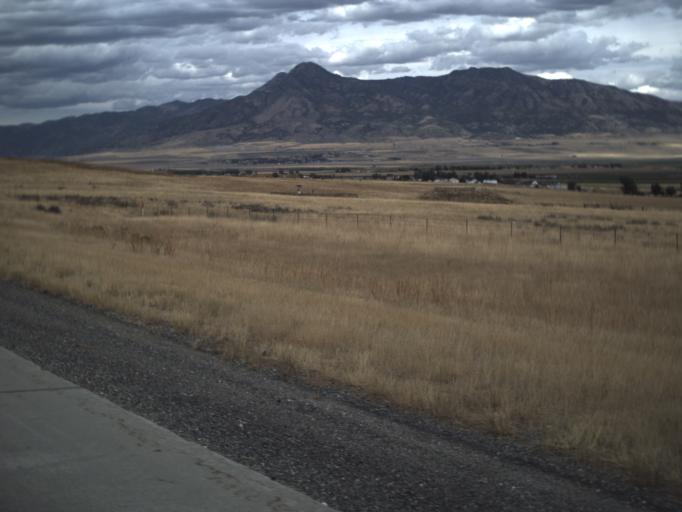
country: US
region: Utah
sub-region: Box Elder County
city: Garland
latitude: 41.7860
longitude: -112.1713
